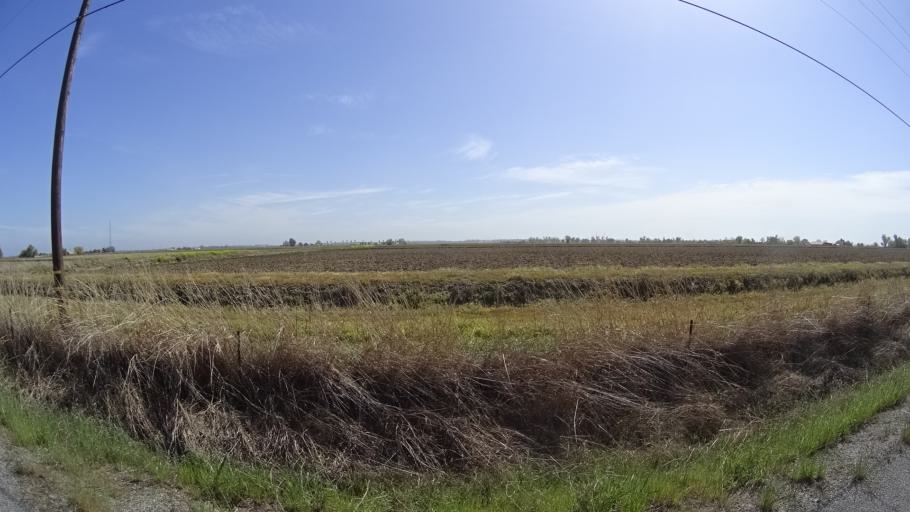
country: US
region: California
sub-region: Glenn County
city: Willows
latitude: 39.5900
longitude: -122.0558
